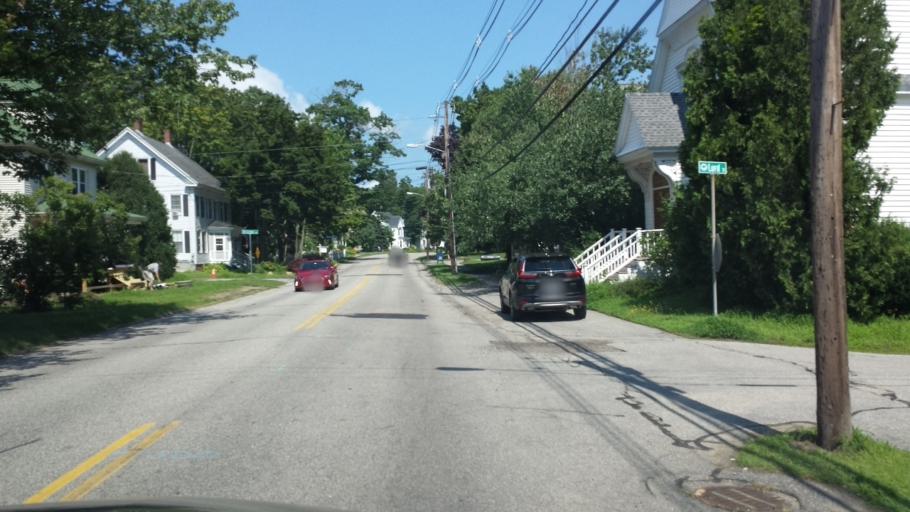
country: US
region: Maine
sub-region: York County
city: Kennebunk
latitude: 43.3874
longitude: -70.5438
